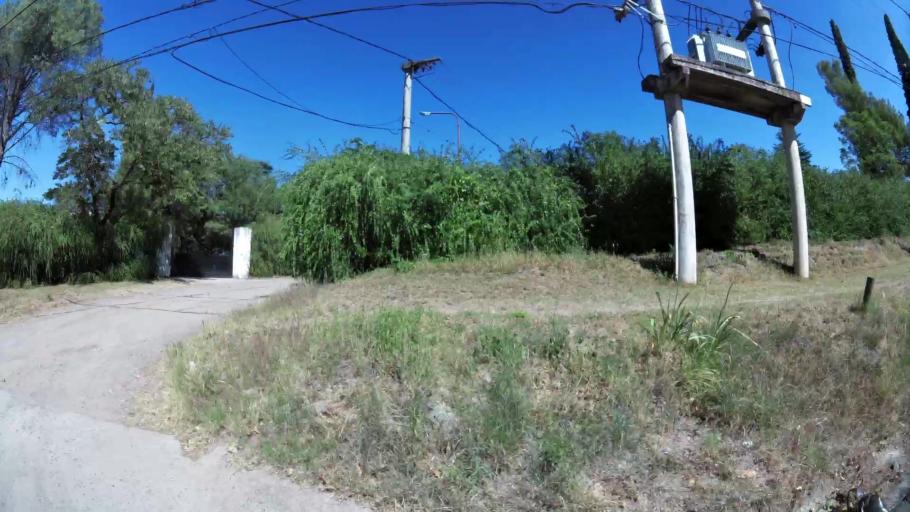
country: AR
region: Cordoba
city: Villa Allende
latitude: -31.2919
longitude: -64.2873
